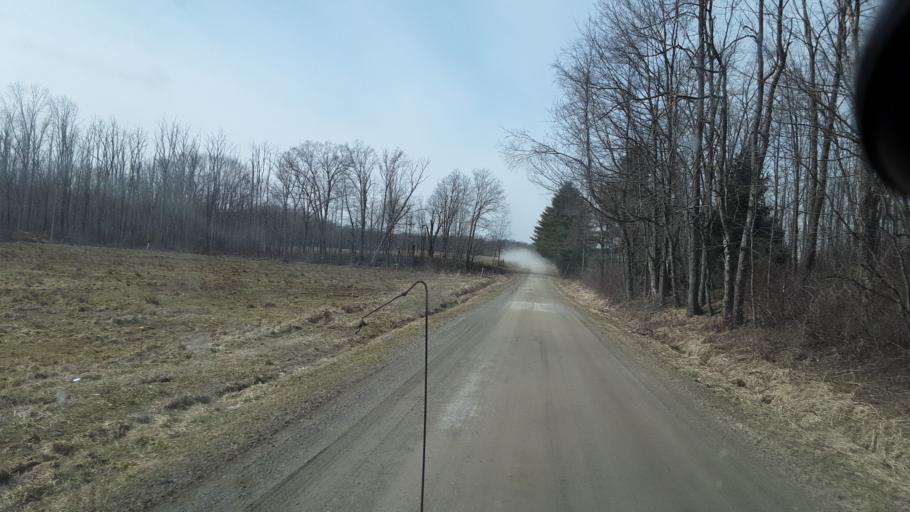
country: US
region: Ohio
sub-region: Ashtabula County
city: Andover
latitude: 41.6239
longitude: -80.6261
